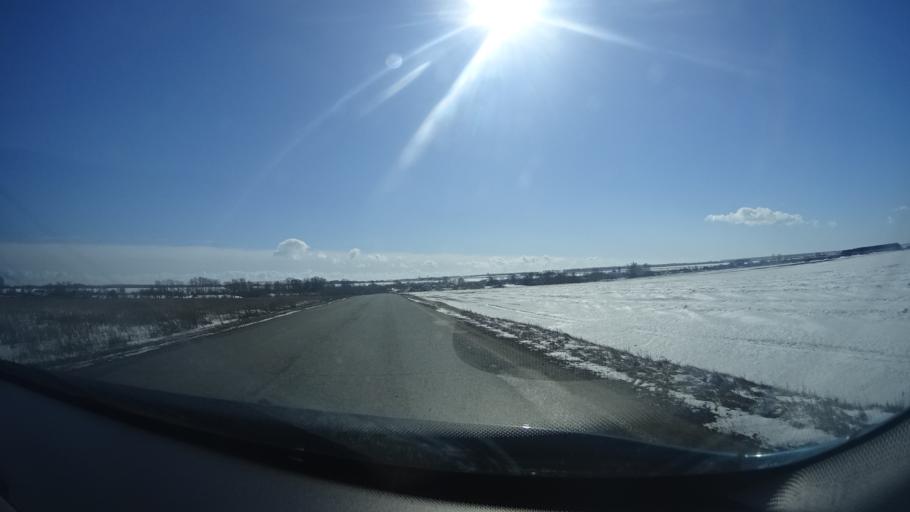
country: RU
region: Bashkortostan
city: Avdon
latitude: 54.5879
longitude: 55.8564
